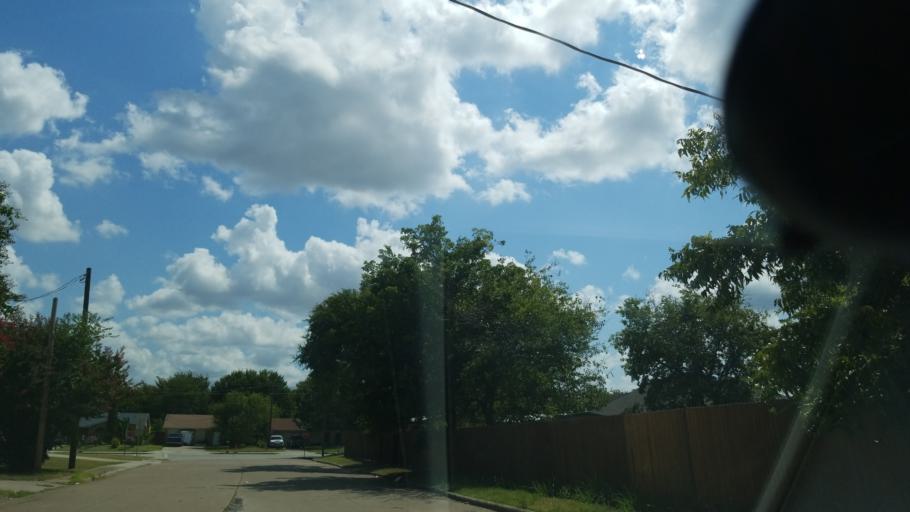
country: US
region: Texas
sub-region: Dallas County
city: Grand Prairie
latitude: 32.7163
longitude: -96.9870
